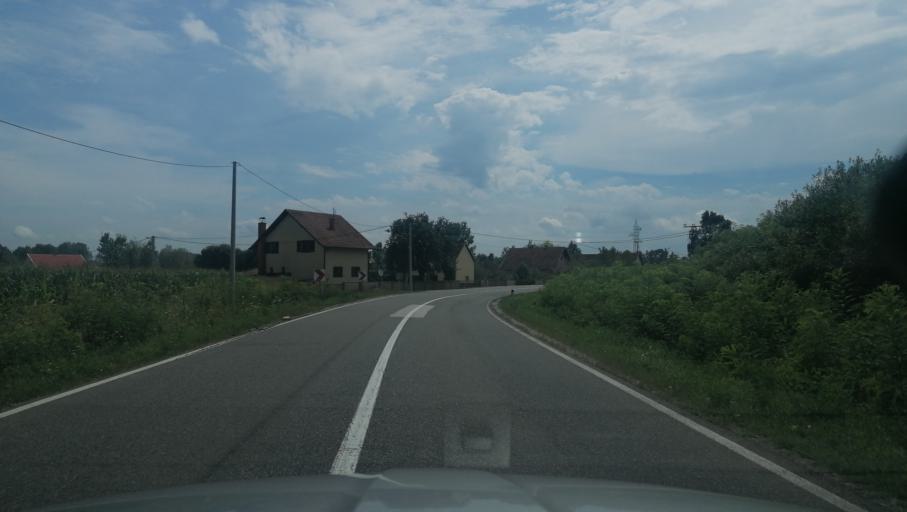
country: BA
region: Republika Srpska
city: Bosanski Samac
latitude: 45.0215
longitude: 18.5169
